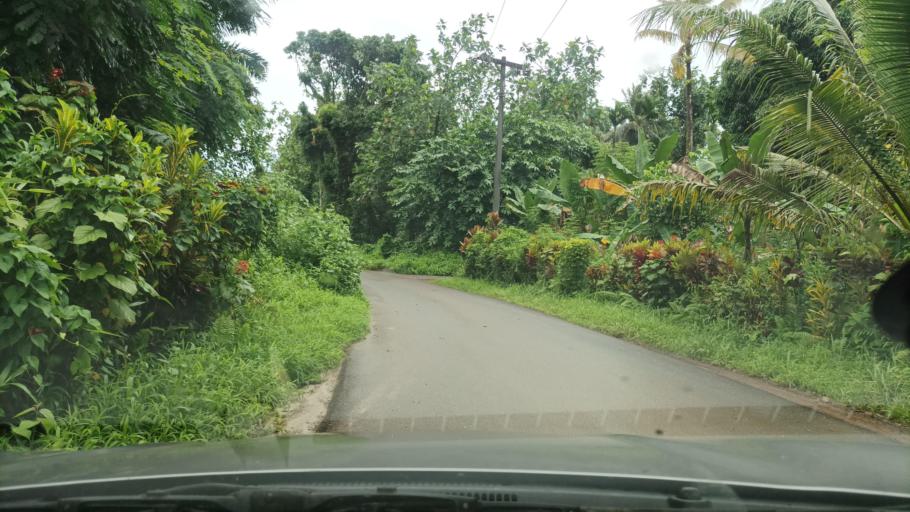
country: FM
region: Pohnpei
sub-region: Madolenihm Municipality
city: Madolenihm Municipality Government
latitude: 6.8172
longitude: 158.2973
